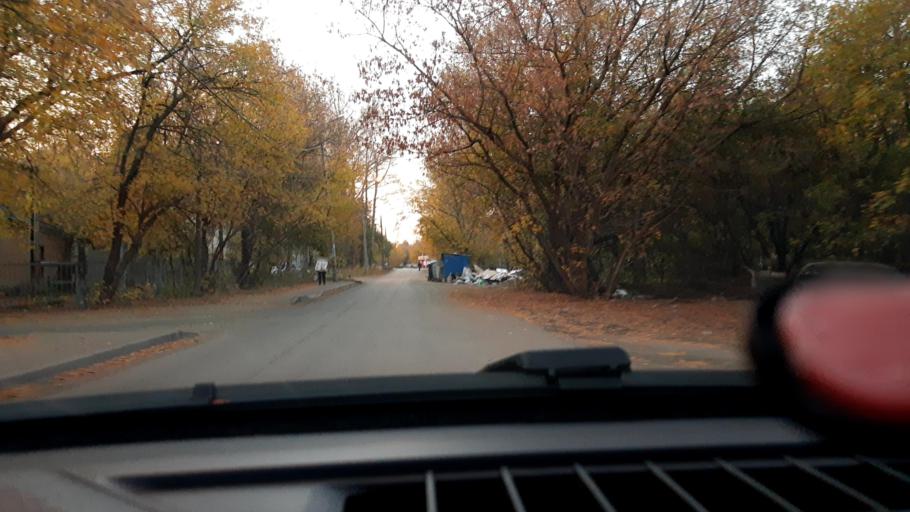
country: RU
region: Nizjnij Novgorod
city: Nizhniy Novgorod
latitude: 56.3044
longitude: 43.8802
